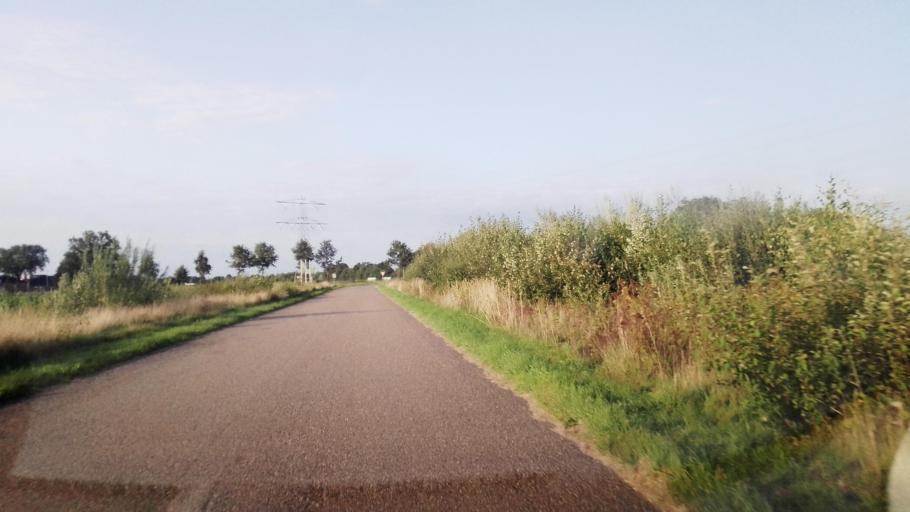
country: NL
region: Limburg
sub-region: Gemeente Peel en Maas
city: Maasbree
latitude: 51.4257
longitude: 6.0982
